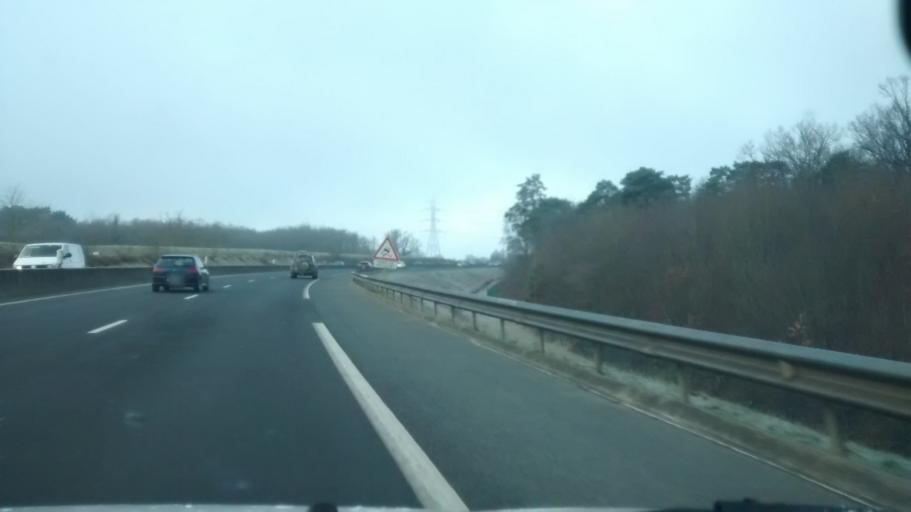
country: FR
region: Centre
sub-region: Departement d'Indre-et-Loire
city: Chambray-les-Tours
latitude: 47.3220
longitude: 0.7007
